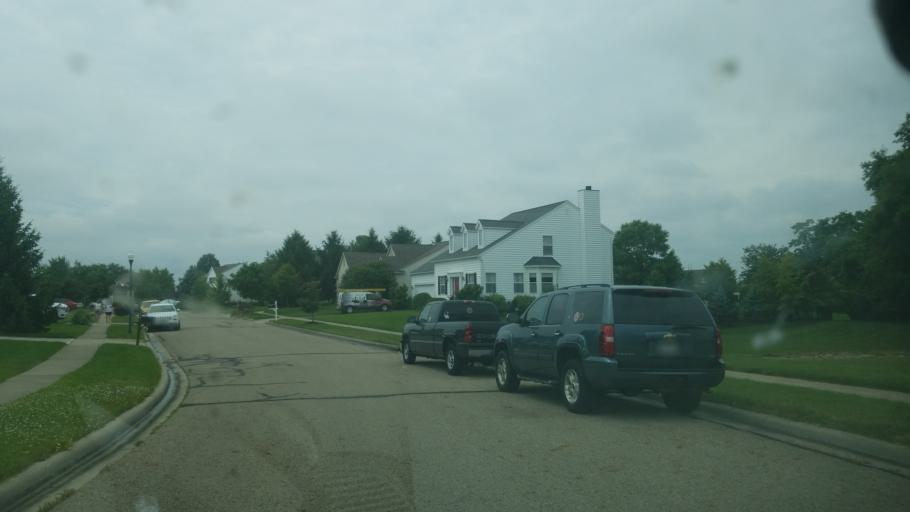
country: US
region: Ohio
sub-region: Franklin County
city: Reynoldsburg
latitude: 40.0092
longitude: -82.7637
